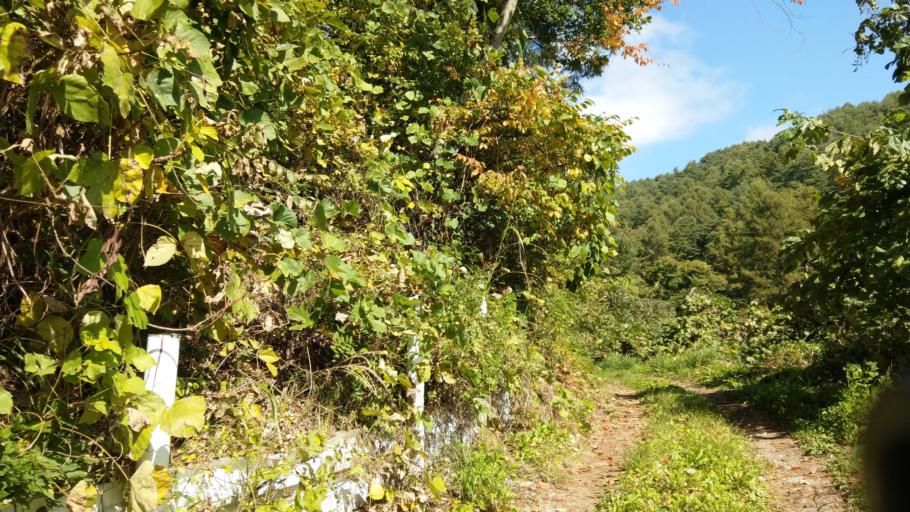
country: JP
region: Nagano
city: Komoro
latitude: 36.3603
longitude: 138.4345
